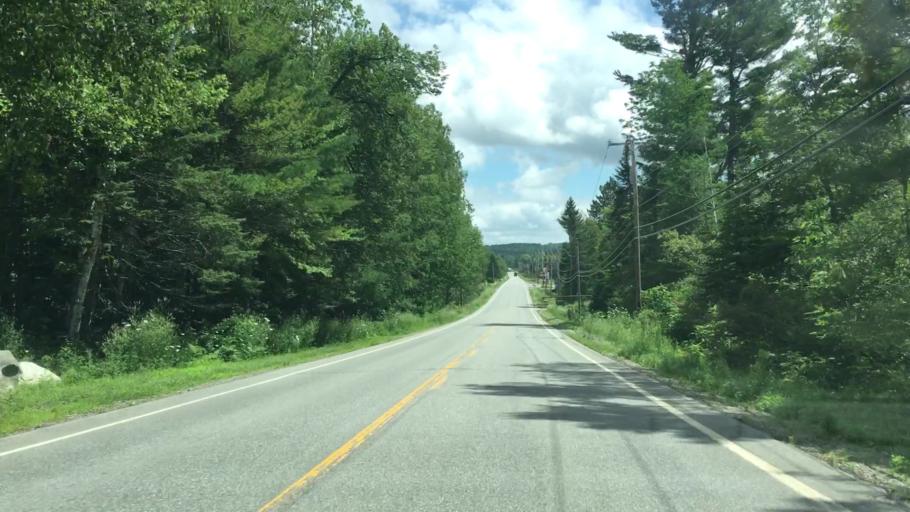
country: US
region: Maine
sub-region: Penobscot County
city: Carmel
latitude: 44.8074
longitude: -68.9921
